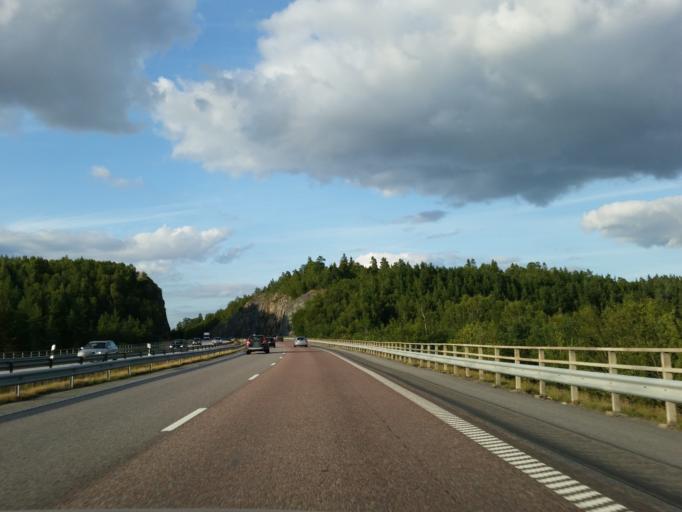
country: SE
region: Stockholm
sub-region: Sodertalje Kommun
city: Pershagen
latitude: 59.1300
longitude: 17.6413
